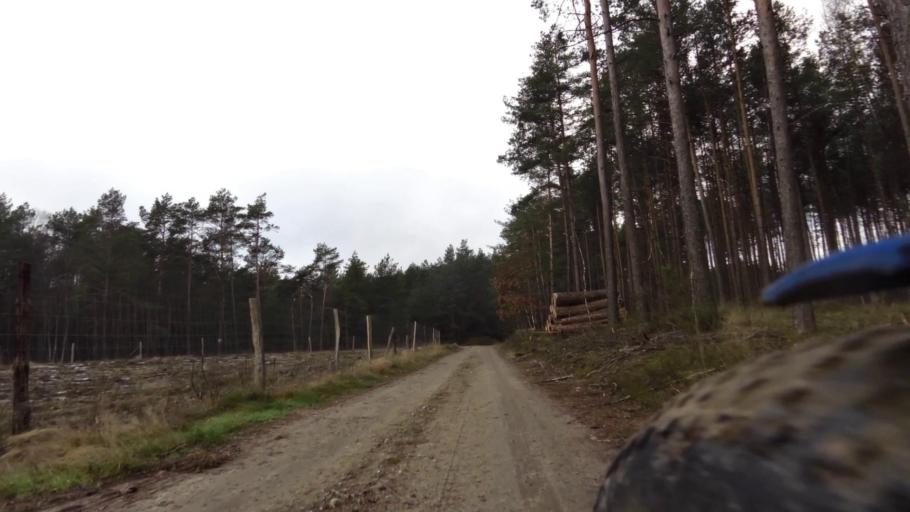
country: PL
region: West Pomeranian Voivodeship
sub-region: Powiat szczecinecki
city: Borne Sulinowo
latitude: 53.6073
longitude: 16.6399
